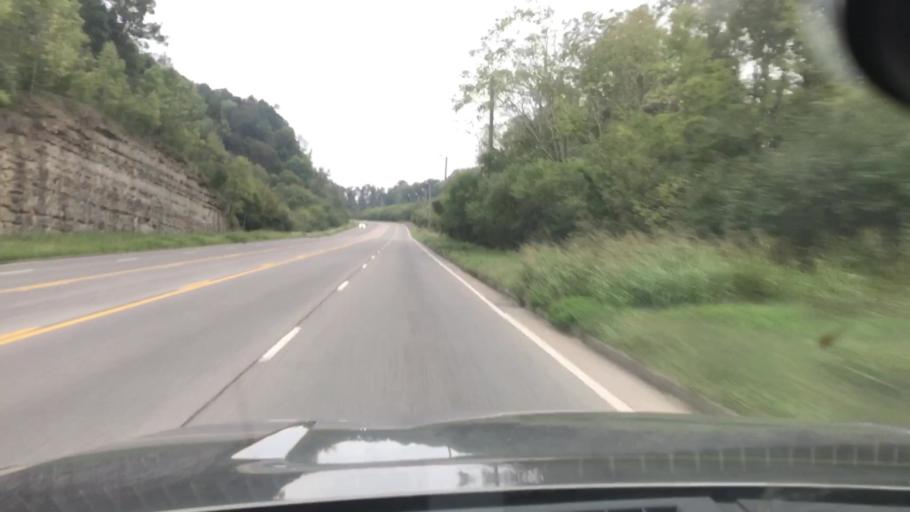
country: US
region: Tennessee
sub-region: Davidson County
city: Belle Meade
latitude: 36.0965
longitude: -86.9247
